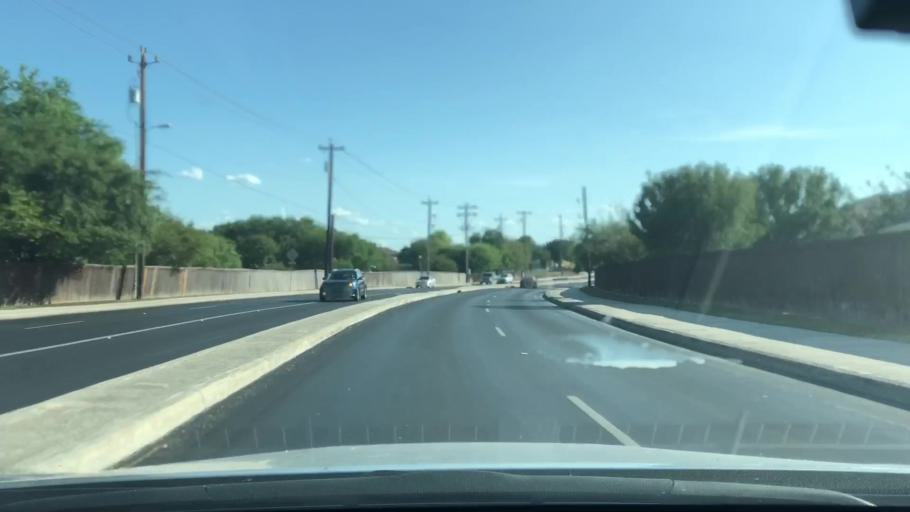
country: US
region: Texas
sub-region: Bexar County
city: Kirby
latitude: 29.4736
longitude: -98.3457
